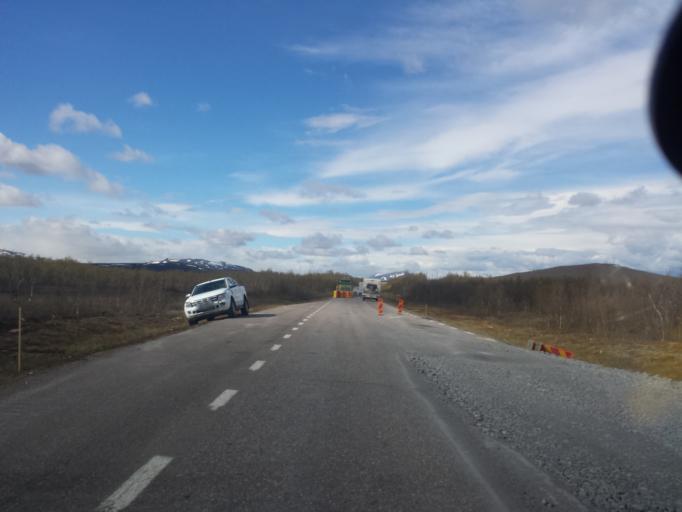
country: SE
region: Norrbotten
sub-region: Kiruna Kommun
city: Kiruna
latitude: 68.0134
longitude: 19.8417
